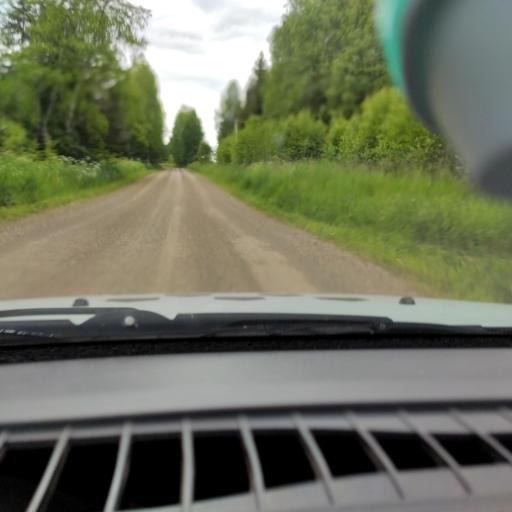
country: RU
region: Perm
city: Suksun
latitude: 57.2054
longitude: 57.6281
